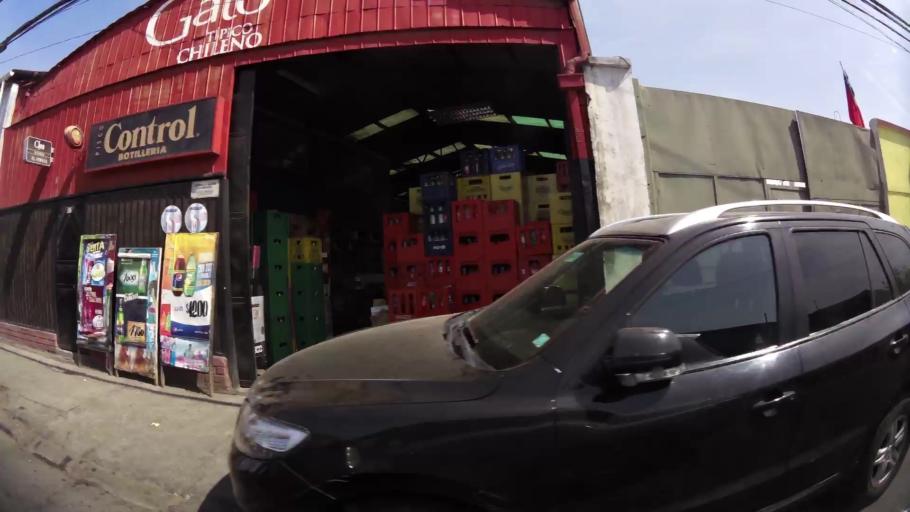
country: CL
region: Santiago Metropolitan
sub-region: Provincia de Santiago
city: Lo Prado
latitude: -33.4362
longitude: -70.7675
